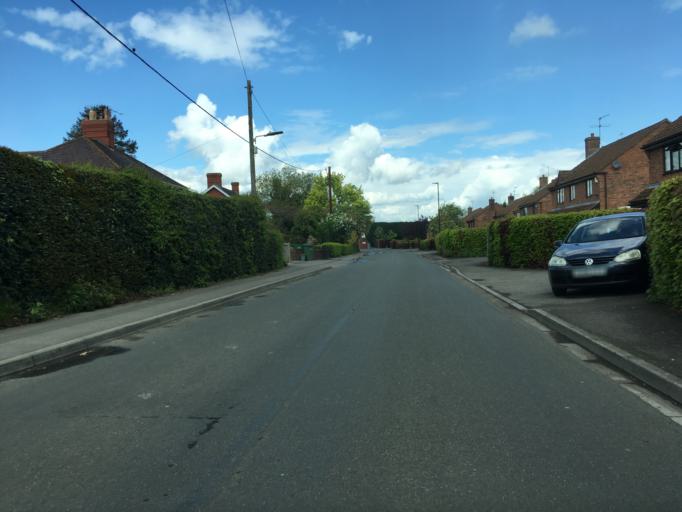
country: GB
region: England
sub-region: Gloucestershire
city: Dursley
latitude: 51.6958
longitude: -2.3570
